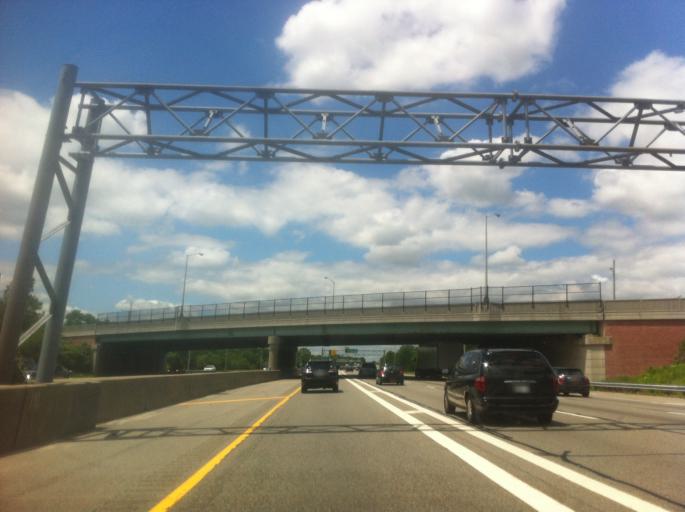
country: US
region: New York
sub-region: Suffolk County
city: Islandia
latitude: 40.8094
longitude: -73.1588
